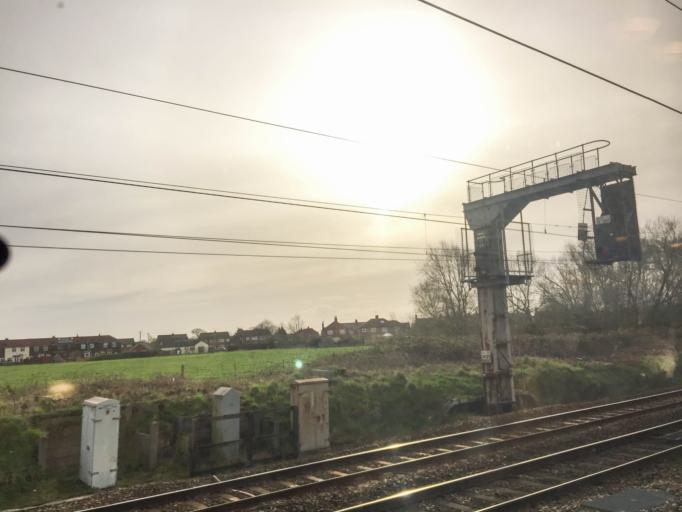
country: GB
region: England
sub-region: Cheshire East
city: Crewe
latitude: 53.1141
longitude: -2.4470
